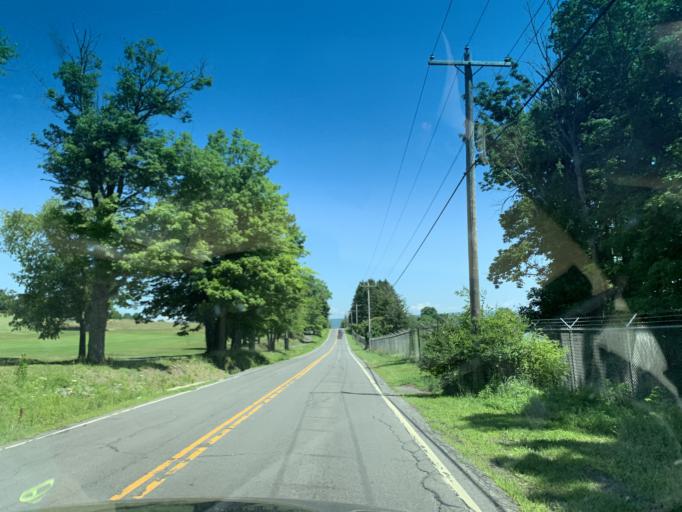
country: US
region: New York
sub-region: Oneida County
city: Utica
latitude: 43.0737
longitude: -75.2378
